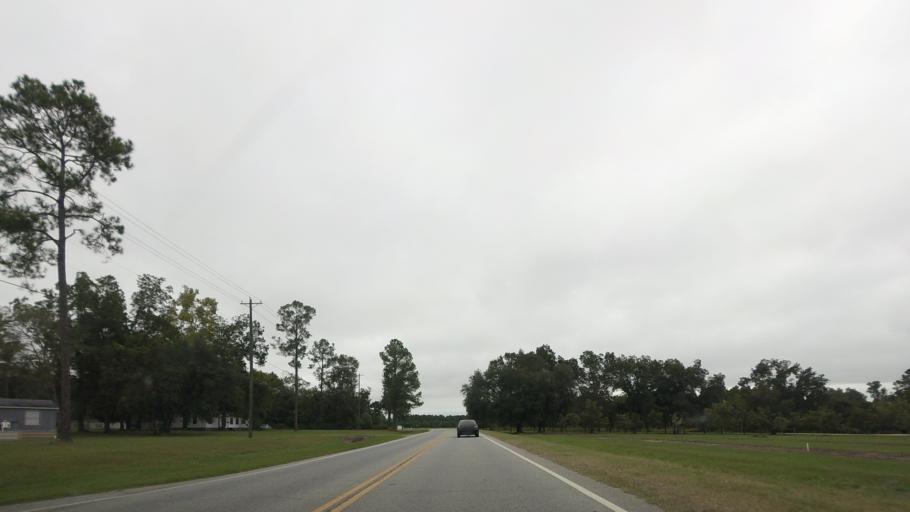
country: US
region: Georgia
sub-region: Berrien County
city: Ray City
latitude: 31.0045
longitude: -83.1986
